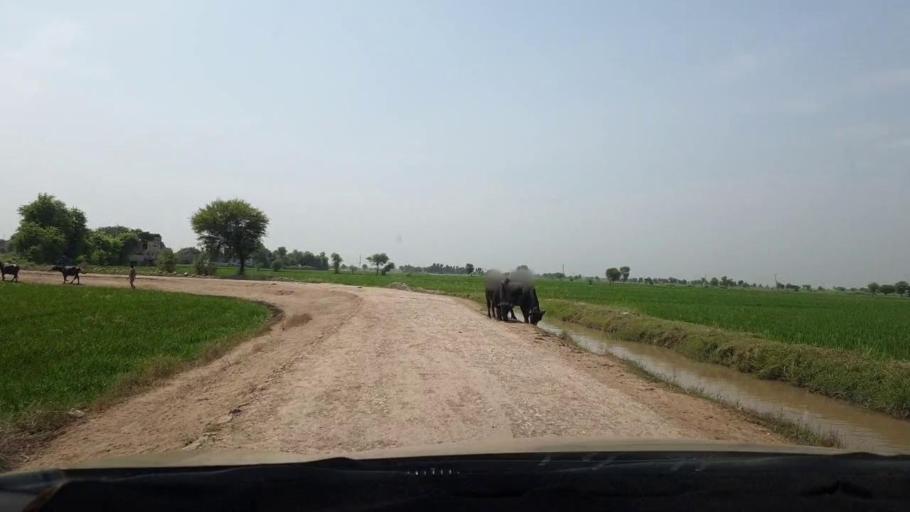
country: PK
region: Sindh
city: Naudero
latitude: 27.6504
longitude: 68.2598
